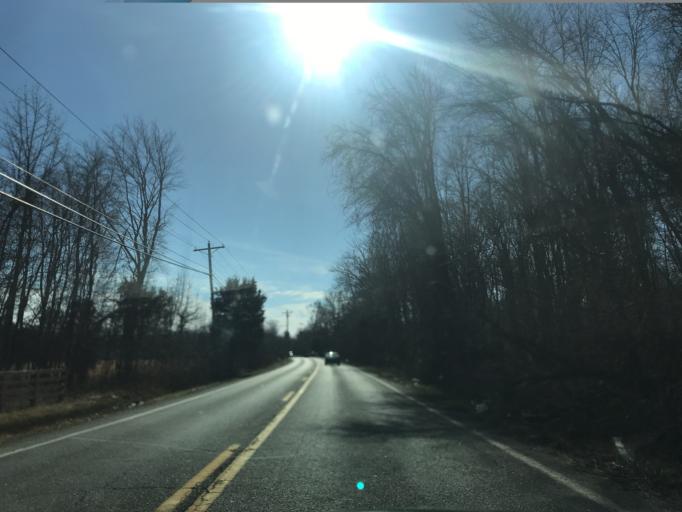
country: US
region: Maryland
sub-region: Charles County
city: Bennsville
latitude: 38.5806
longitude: -77.0297
